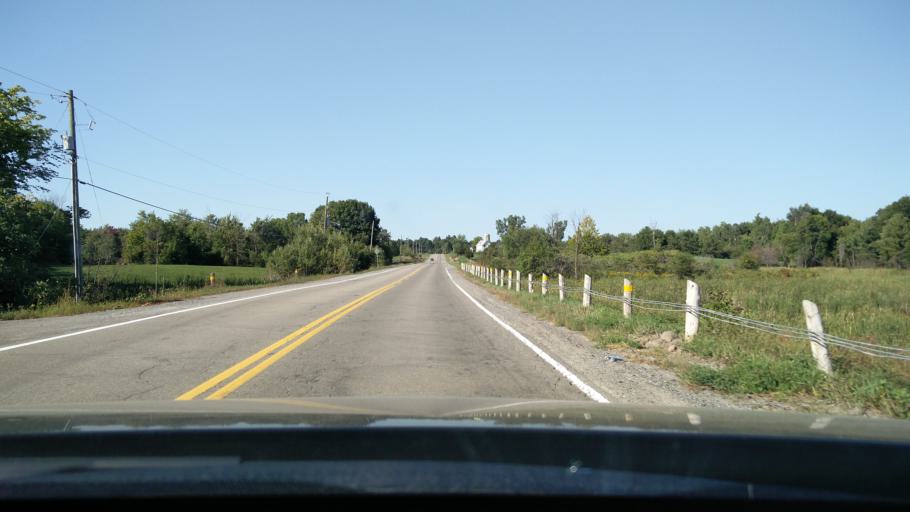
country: CA
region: Ontario
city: Perth
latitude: 44.6975
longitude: -76.4011
